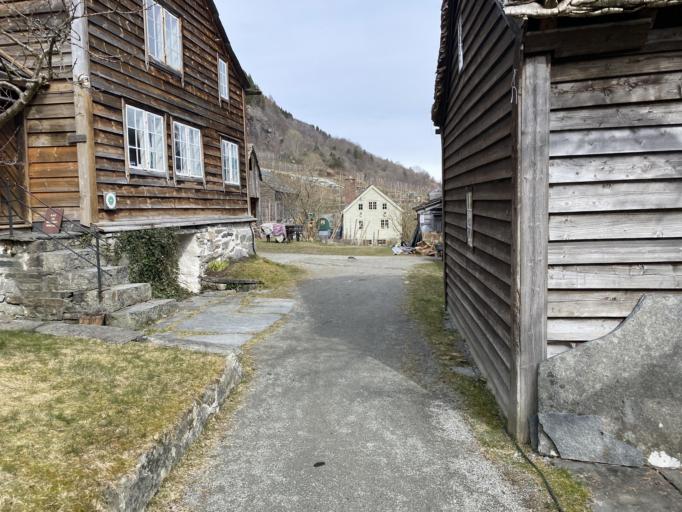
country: NO
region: Hordaland
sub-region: Ullensvang
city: Kinsarvik
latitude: 60.3003
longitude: 6.6025
